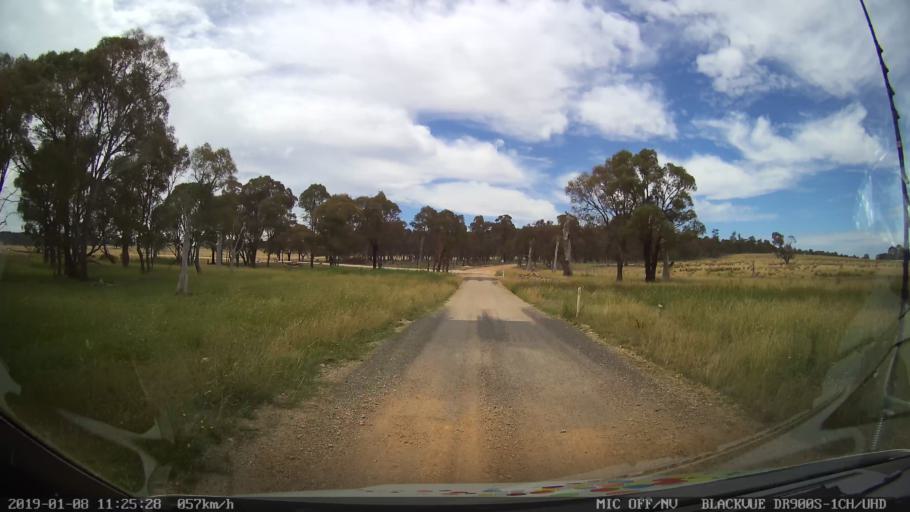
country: AU
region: New South Wales
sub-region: Guyra
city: Guyra
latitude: -30.2738
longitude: 151.5611
